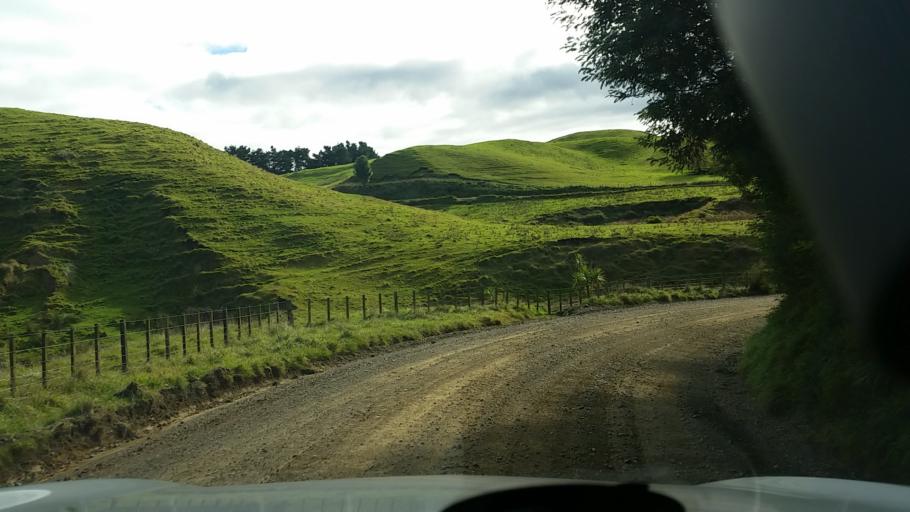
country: NZ
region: Hawke's Bay
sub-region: Napier City
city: Napier
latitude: -39.1071
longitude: 176.8897
